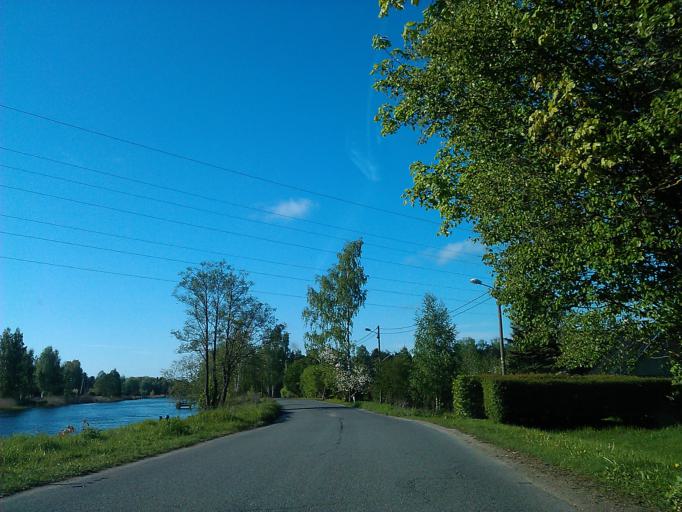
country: LV
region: Riga
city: Bergi
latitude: 57.0050
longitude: 24.2707
